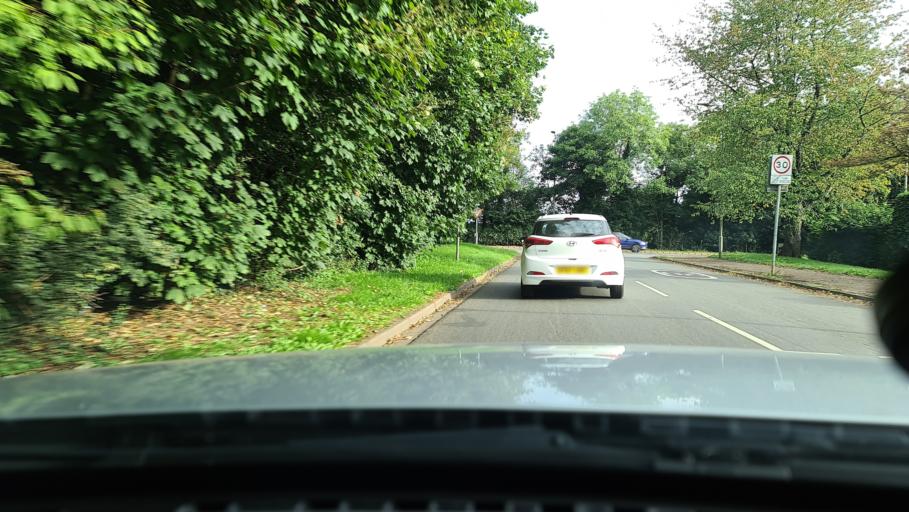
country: GB
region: England
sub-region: Oxfordshire
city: Hanwell
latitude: 52.0705
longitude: -1.3685
